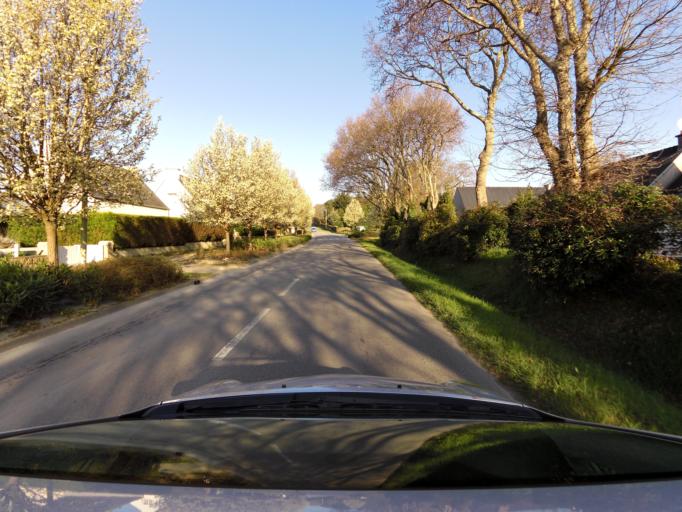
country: FR
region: Brittany
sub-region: Departement du Morbihan
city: Ploemeur
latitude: 47.7373
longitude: -3.4381
